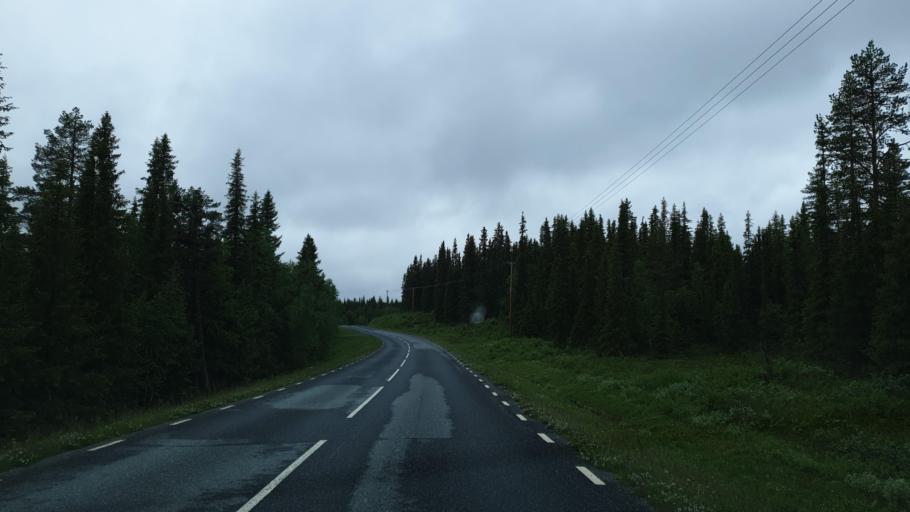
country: SE
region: Vaesterbotten
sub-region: Vilhelmina Kommun
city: Sjoberg
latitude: 65.2374
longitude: 15.8193
